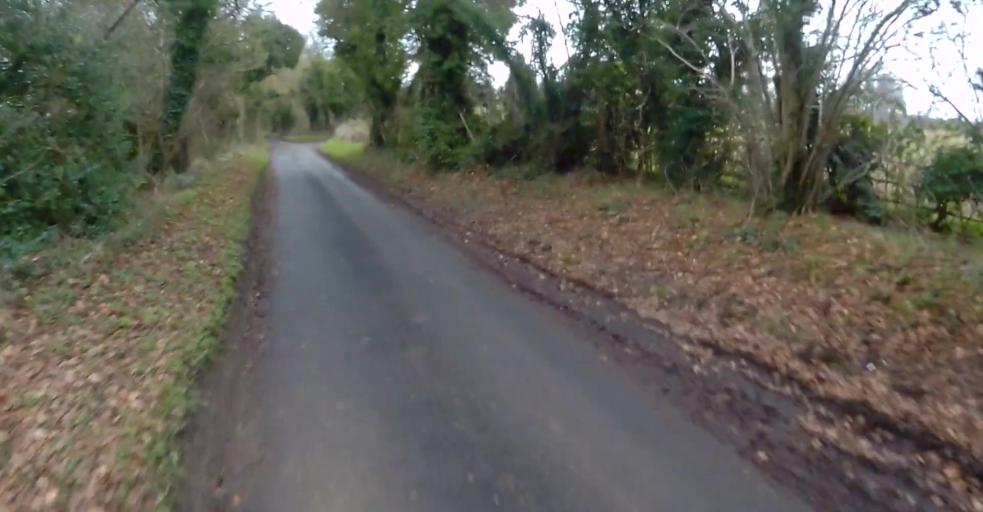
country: GB
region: England
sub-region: Hampshire
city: Overton
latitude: 51.2175
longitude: -1.2178
